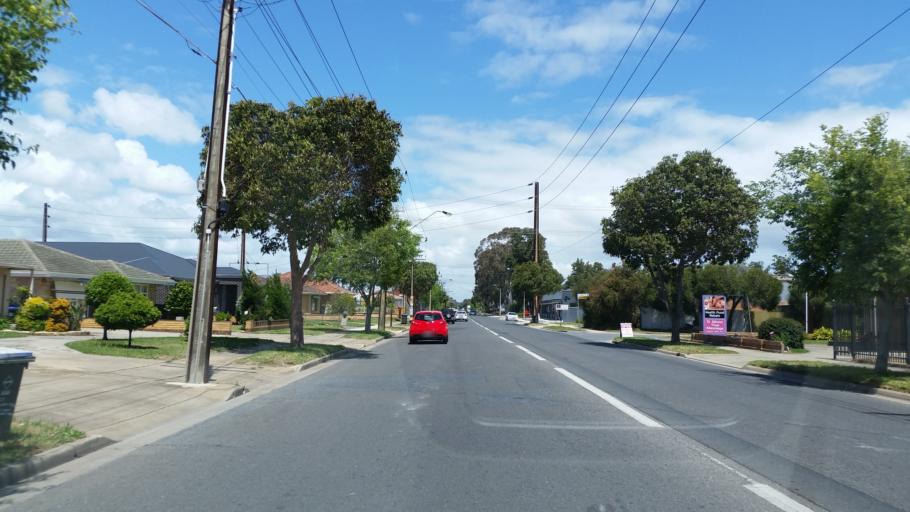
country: AU
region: South Australia
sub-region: Charles Sturt
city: Findon
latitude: -34.9074
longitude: 138.5329
